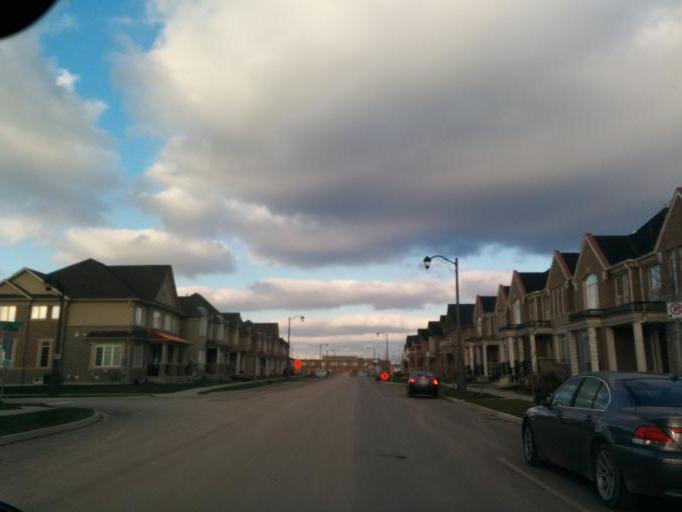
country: CA
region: Ontario
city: Oakville
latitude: 43.4682
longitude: -79.7456
